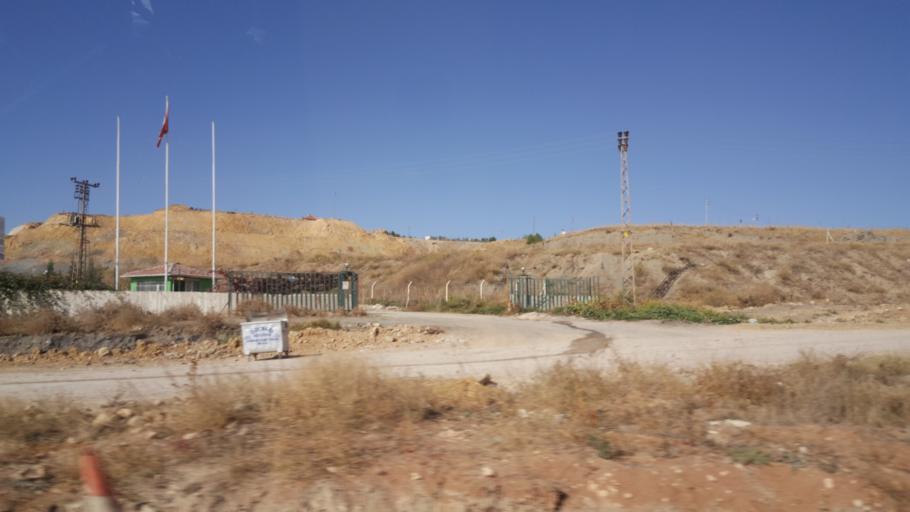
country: TR
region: Ankara
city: Ikizce
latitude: 39.6583
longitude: 32.7283
